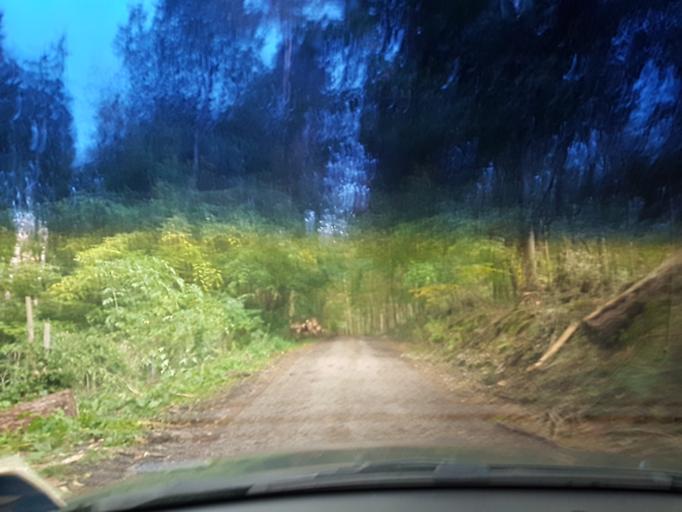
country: DE
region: Bavaria
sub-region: Regierungsbezirk Mittelfranken
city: Markt Taschendorf
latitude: 49.7605
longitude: 10.5385
